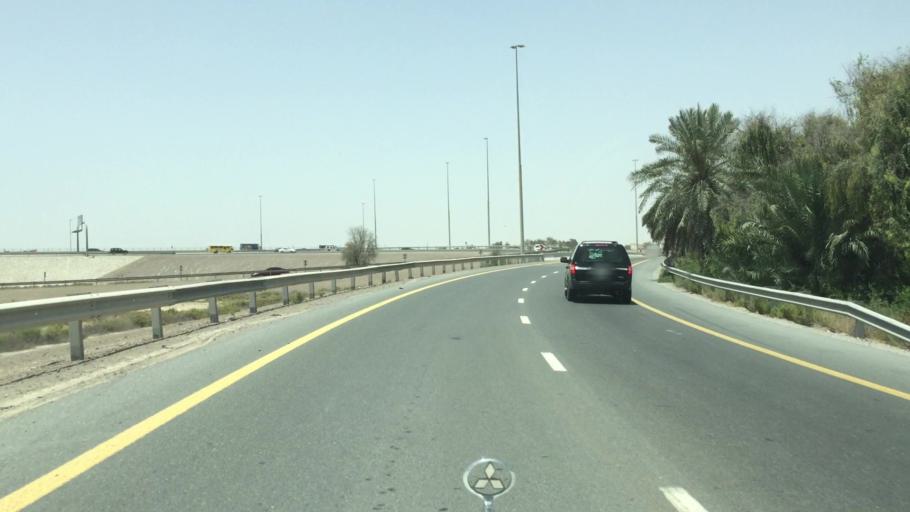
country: AE
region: Dubai
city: Dubai
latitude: 25.1182
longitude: 55.3673
